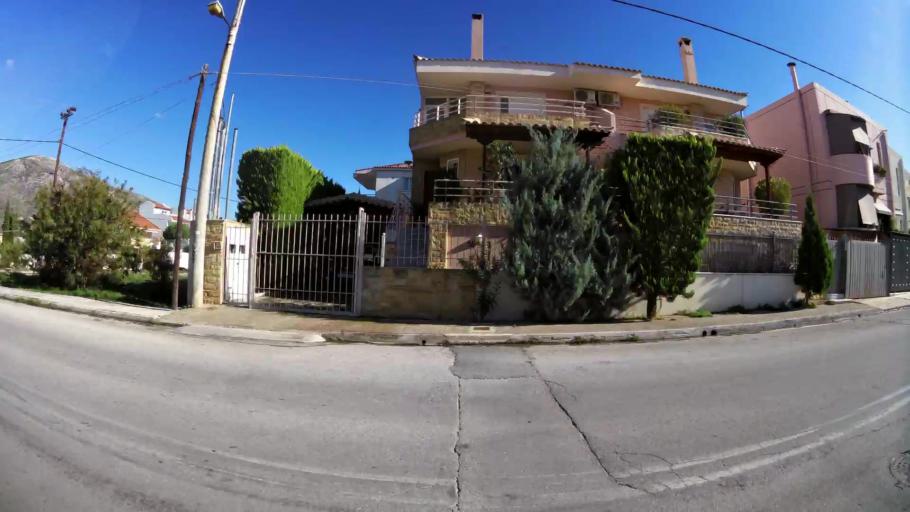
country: GR
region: Attica
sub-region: Nomarchia Anatolikis Attikis
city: Kalyvia Thorikou
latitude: 37.8386
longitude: 23.9338
